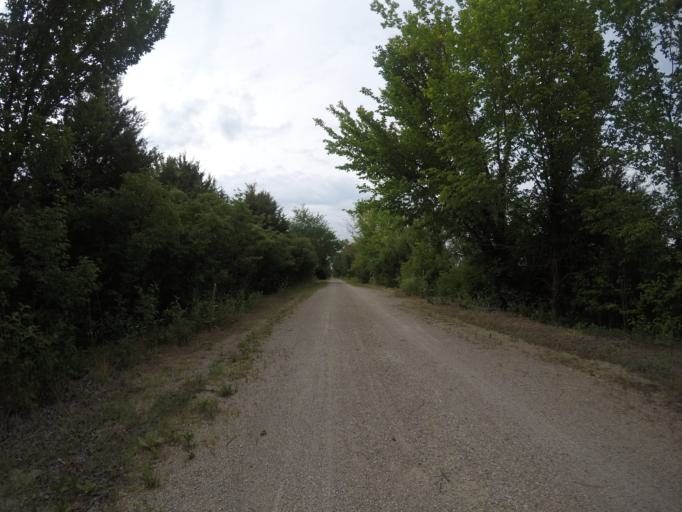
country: US
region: Kansas
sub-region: Franklin County
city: Ottawa
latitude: 38.4968
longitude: -95.2737
